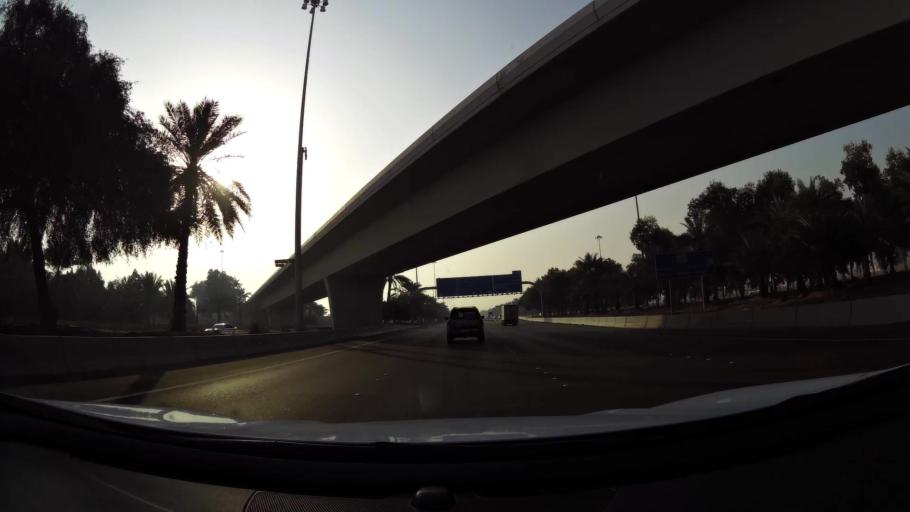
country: AE
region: Abu Dhabi
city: Abu Dhabi
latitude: 24.3890
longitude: 54.5397
